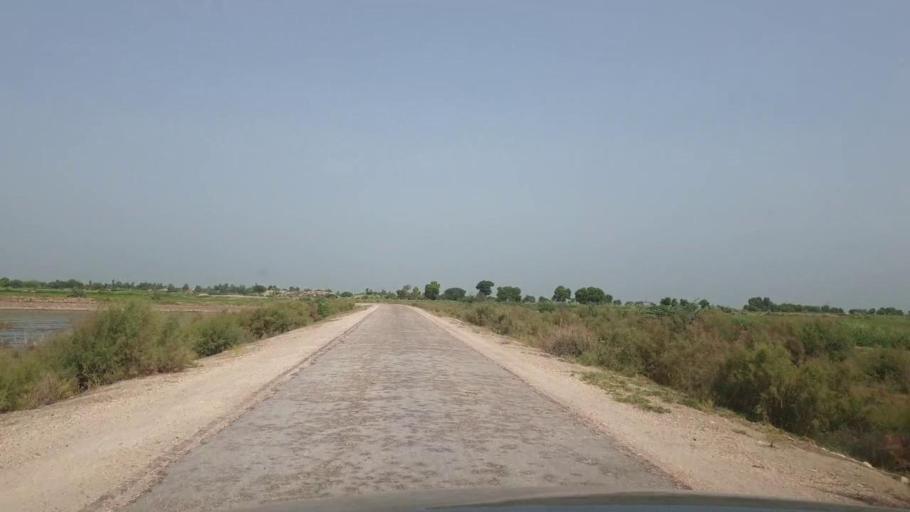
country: PK
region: Sindh
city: Madeji
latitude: 27.8387
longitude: 68.4421
